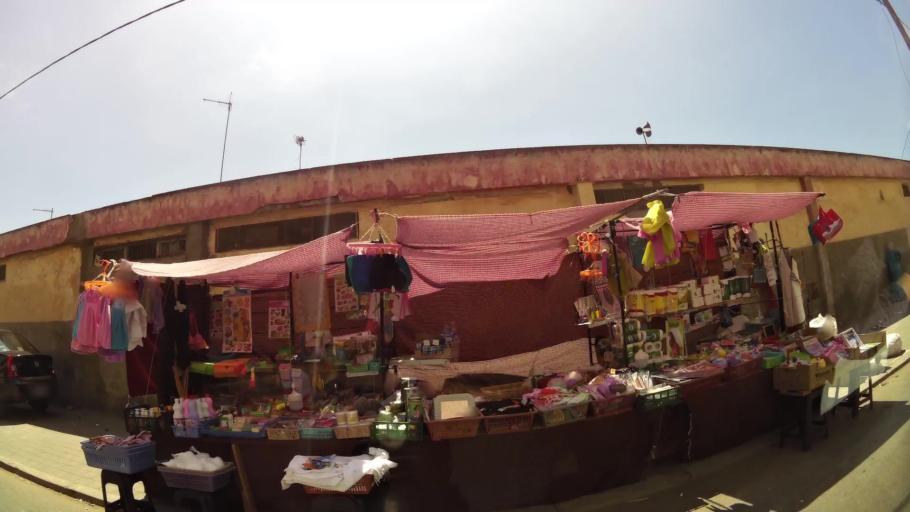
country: MA
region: Gharb-Chrarda-Beni Hssen
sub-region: Kenitra Province
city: Kenitra
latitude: 34.2515
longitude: -6.5504
